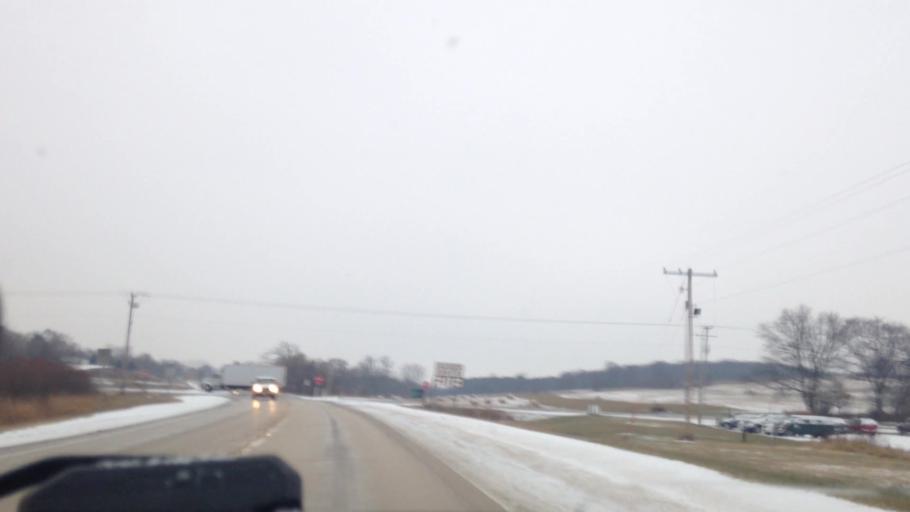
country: US
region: Wisconsin
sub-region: Dodge County
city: Mayville
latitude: 43.4440
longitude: -88.5443
